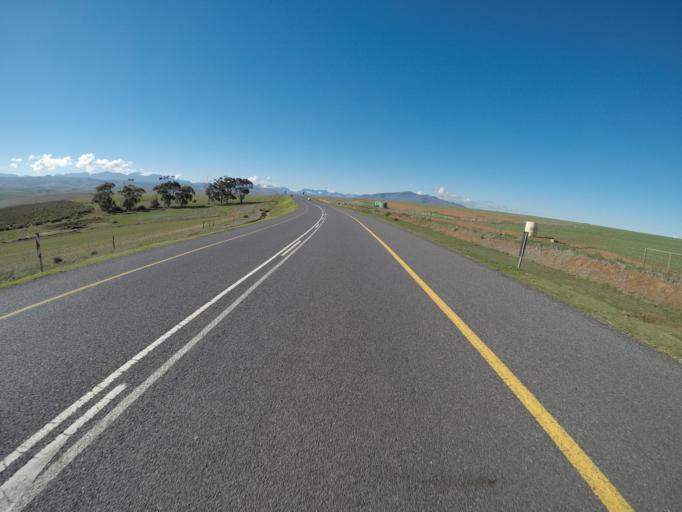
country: ZA
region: Western Cape
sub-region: Overberg District Municipality
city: Caledon
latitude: -34.2204
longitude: 19.3113
